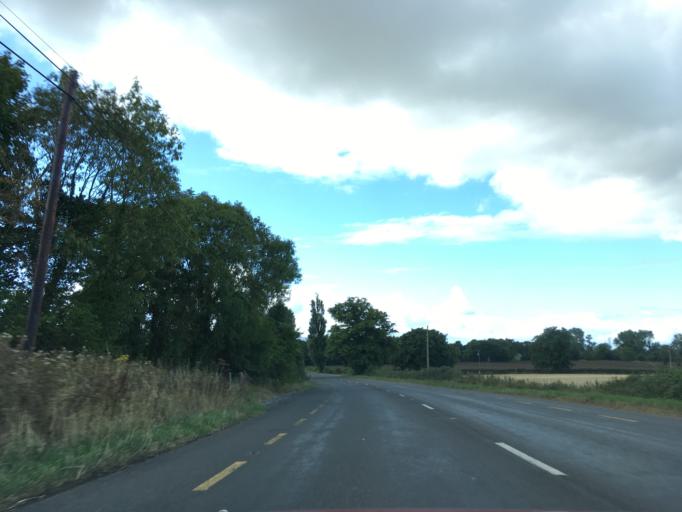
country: IE
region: Munster
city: Cahir
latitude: 52.4100
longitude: -7.8947
